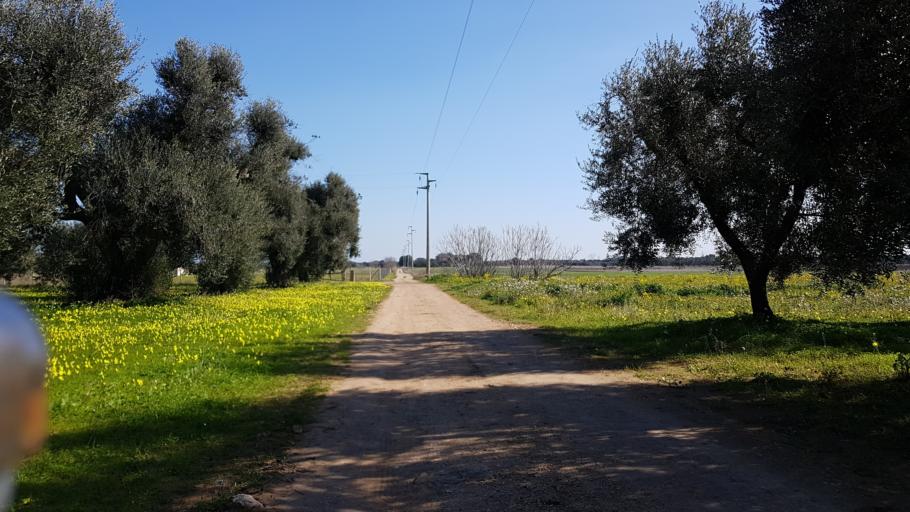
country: IT
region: Apulia
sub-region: Provincia di Brindisi
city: Mesagne
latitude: 40.6118
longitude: 17.7970
